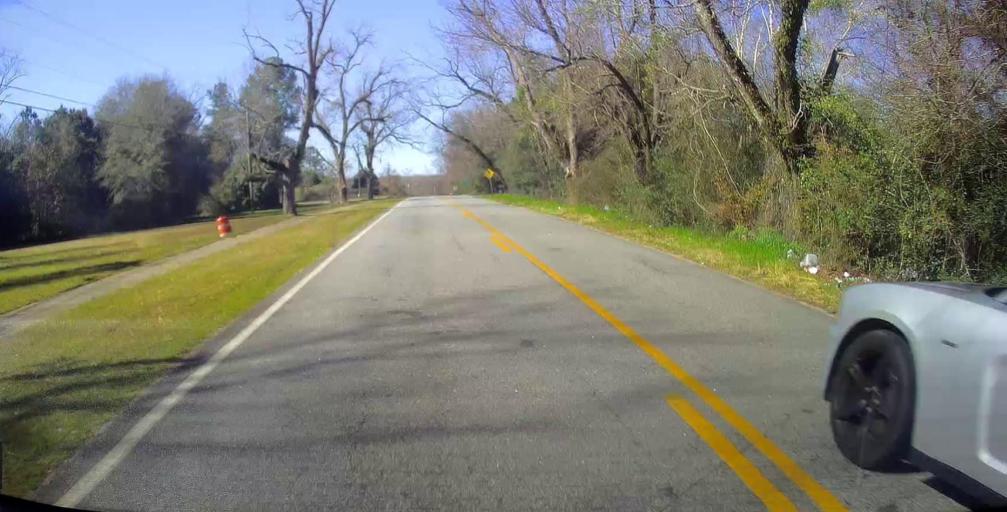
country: US
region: Georgia
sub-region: Macon County
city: Montezuma
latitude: 32.2819
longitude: -84.0296
